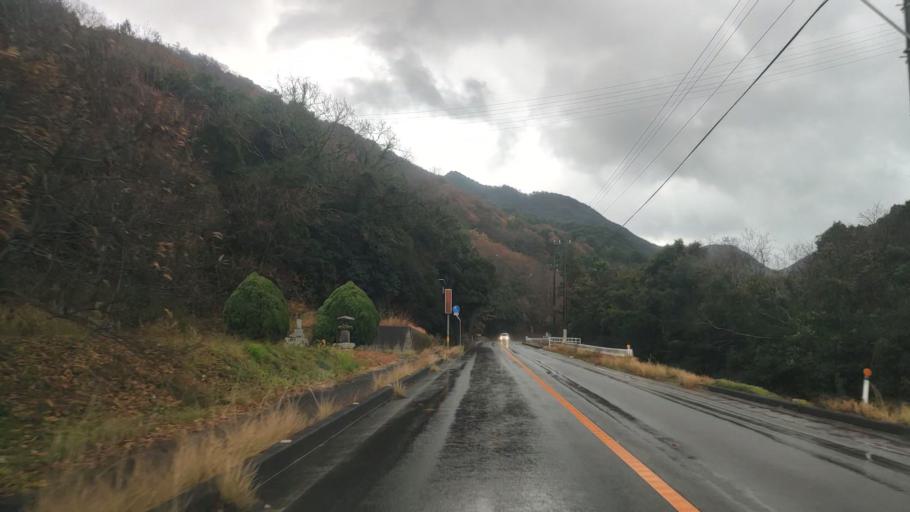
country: JP
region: Tokushima
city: Kamojimacho-jogejima
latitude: 34.1914
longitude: 134.3348
